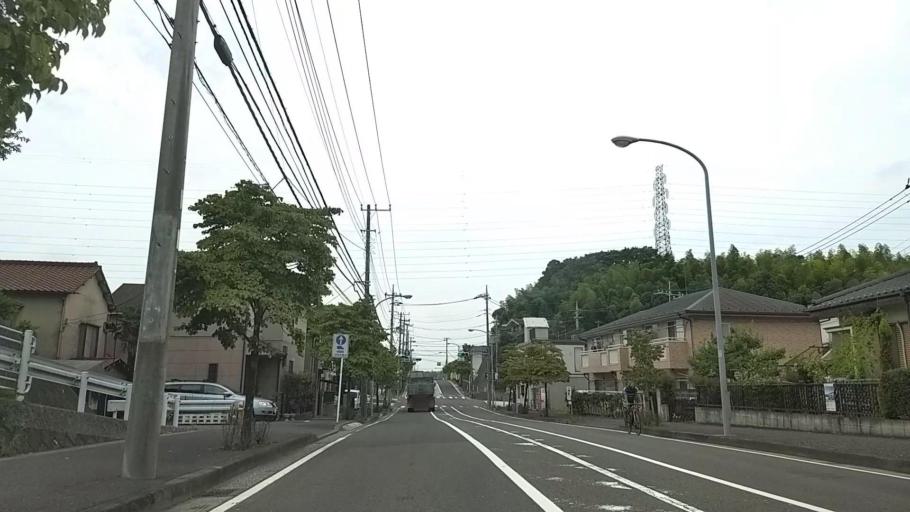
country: JP
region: Kanagawa
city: Yokohama
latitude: 35.5584
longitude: 139.6067
